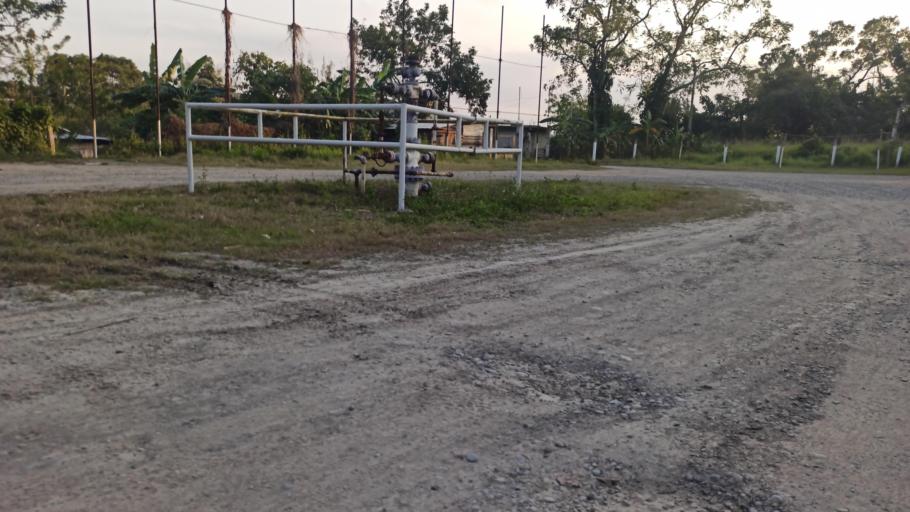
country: MX
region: Veracruz
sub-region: Poza Rica de Hidalgo
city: Arroyo del Maiz Uno
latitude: 20.4769
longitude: -97.3903
